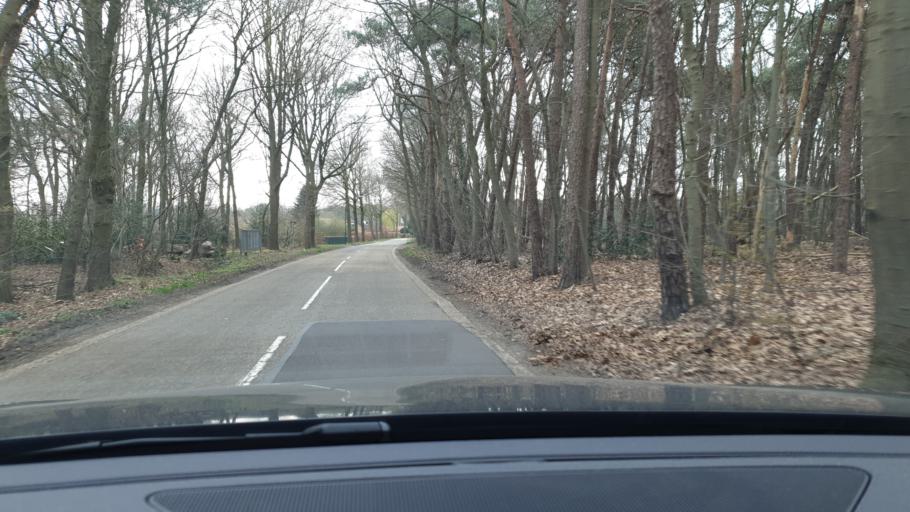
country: NL
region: North Brabant
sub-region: Gemeente Son en Breugel
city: Breugel
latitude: 51.5244
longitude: 5.5128
